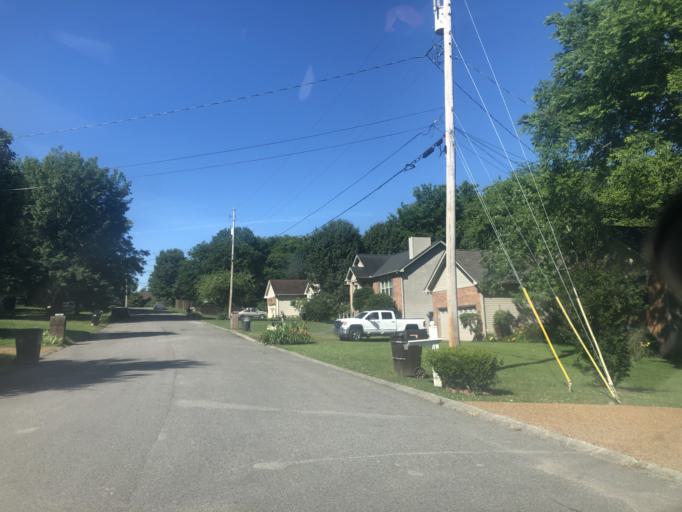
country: US
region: Tennessee
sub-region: Davidson County
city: Lakewood
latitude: 36.2408
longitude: -86.6669
